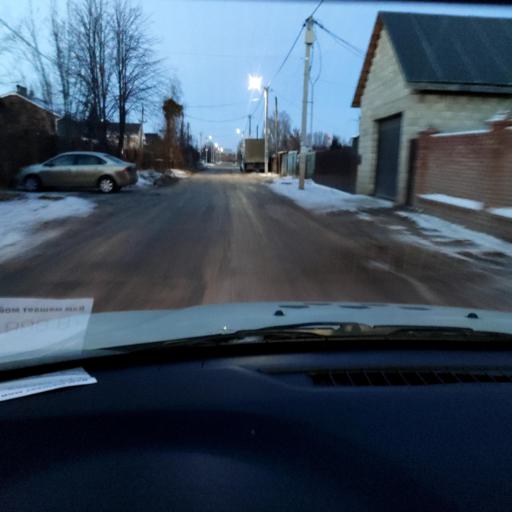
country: RU
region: Samara
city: Tol'yatti
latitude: 53.5656
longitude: 49.3900
